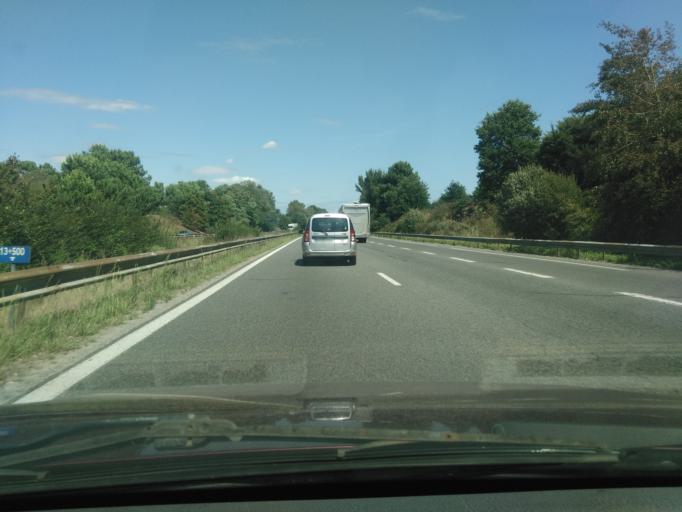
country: FR
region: Aquitaine
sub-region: Departement de la Gironde
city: Le Haillan
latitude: 44.8596
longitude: -0.6603
